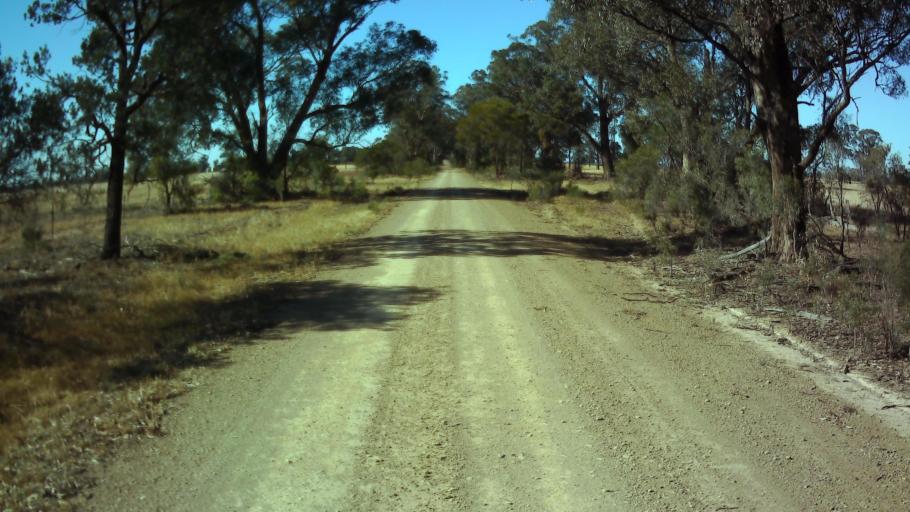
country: AU
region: New South Wales
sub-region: Weddin
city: Grenfell
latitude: -33.9188
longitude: 147.8752
